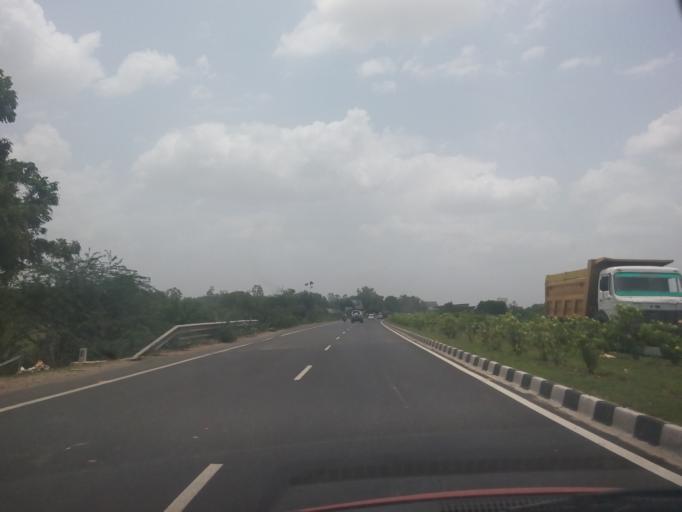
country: IN
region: Gujarat
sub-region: Ahmadabad
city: Sarkhej
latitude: 22.9873
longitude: 72.4487
